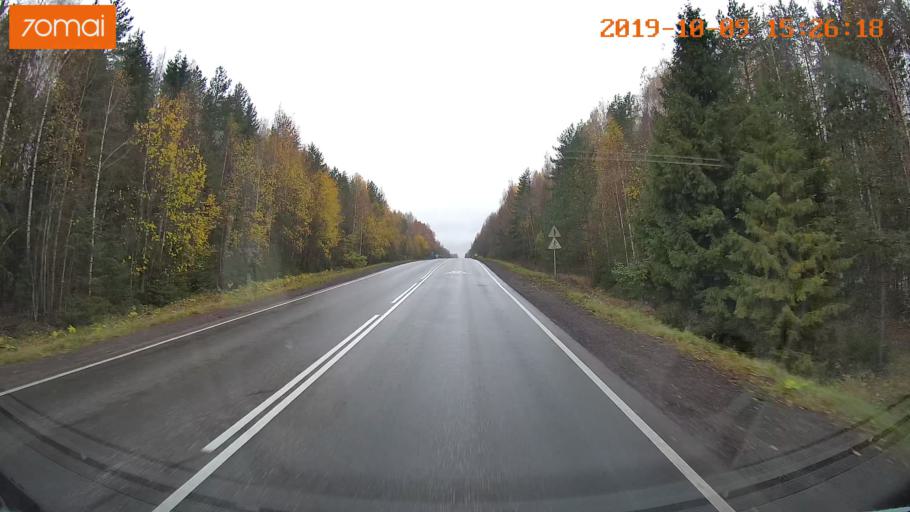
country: RU
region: Kostroma
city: Susanino
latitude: 58.0210
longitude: 41.4074
